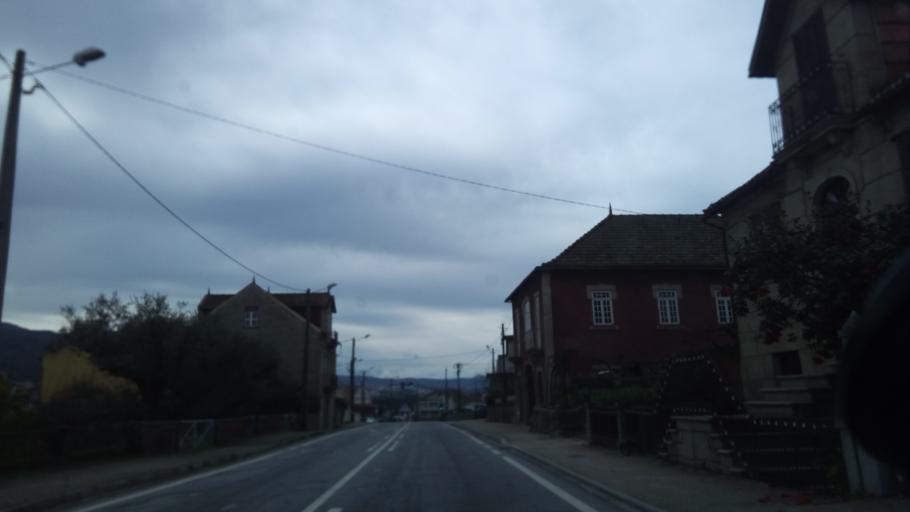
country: PT
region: Guarda
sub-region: Seia
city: Seia
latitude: 40.4673
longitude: -7.6832
